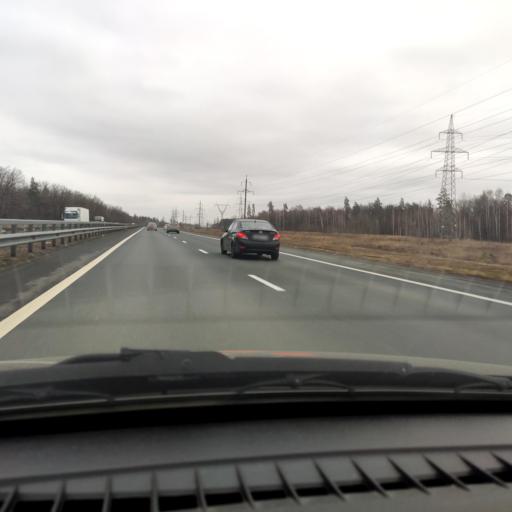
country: RU
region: Samara
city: Pribrezhnyy
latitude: 53.5187
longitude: 49.8033
